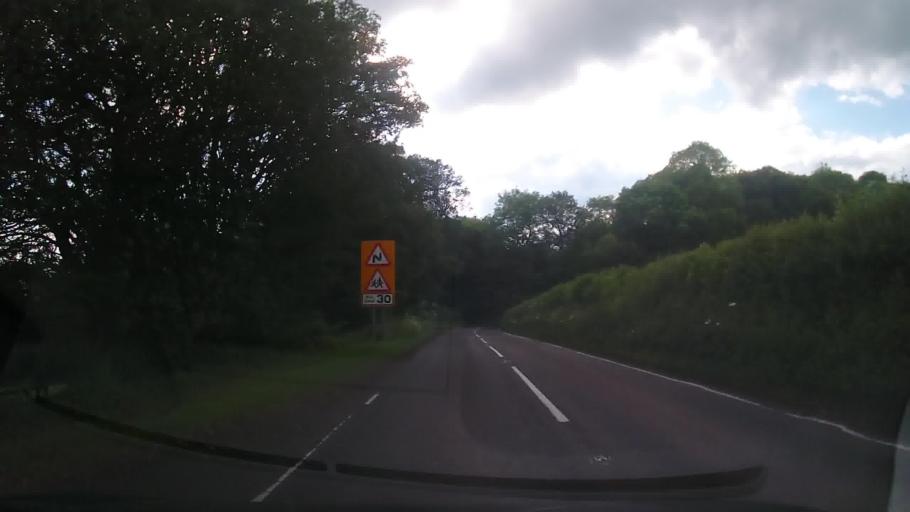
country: GB
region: England
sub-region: Shropshire
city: Much Wenlock
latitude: 52.6414
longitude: -2.5634
